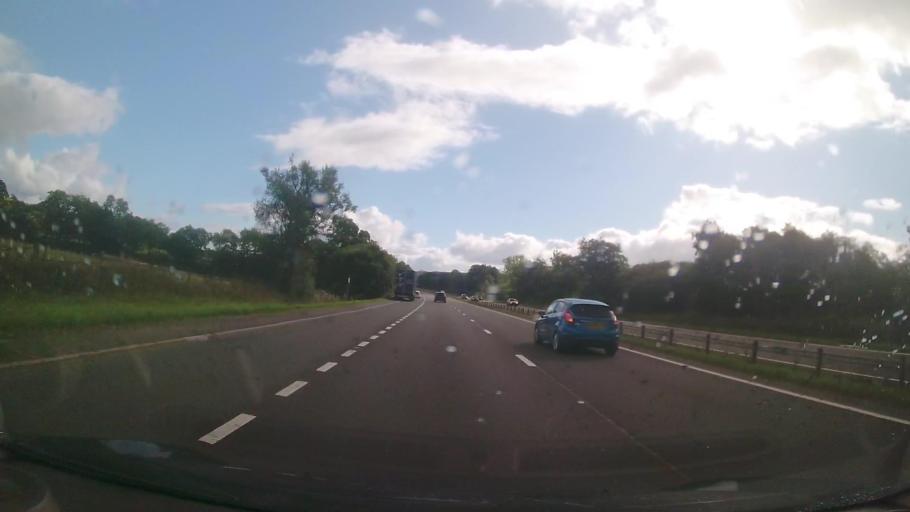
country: GB
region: Wales
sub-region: Carmarthenshire
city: Carmarthen
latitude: 51.8401
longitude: -4.2884
